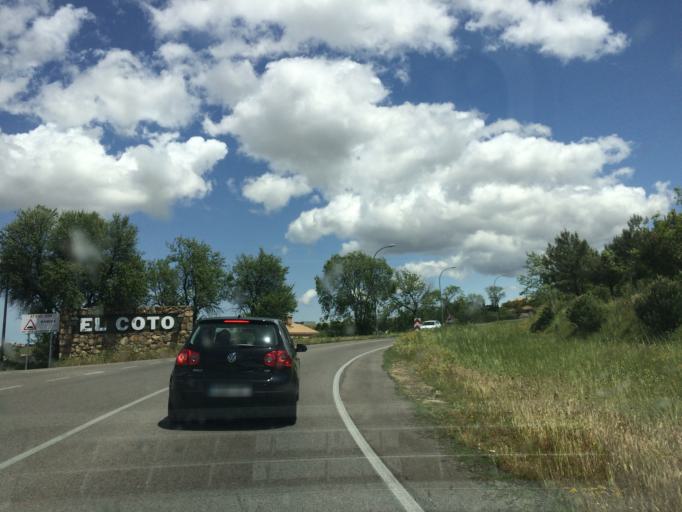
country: ES
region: Madrid
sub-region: Provincia de Madrid
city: Valdeolmos
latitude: 40.6942
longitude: -3.4459
